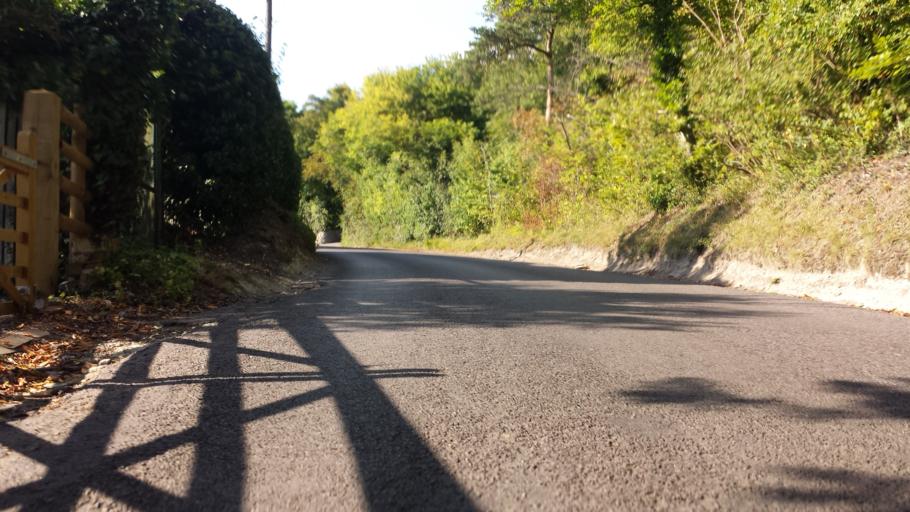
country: GB
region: England
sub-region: Kent
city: Eynsford
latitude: 51.3716
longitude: 0.2066
